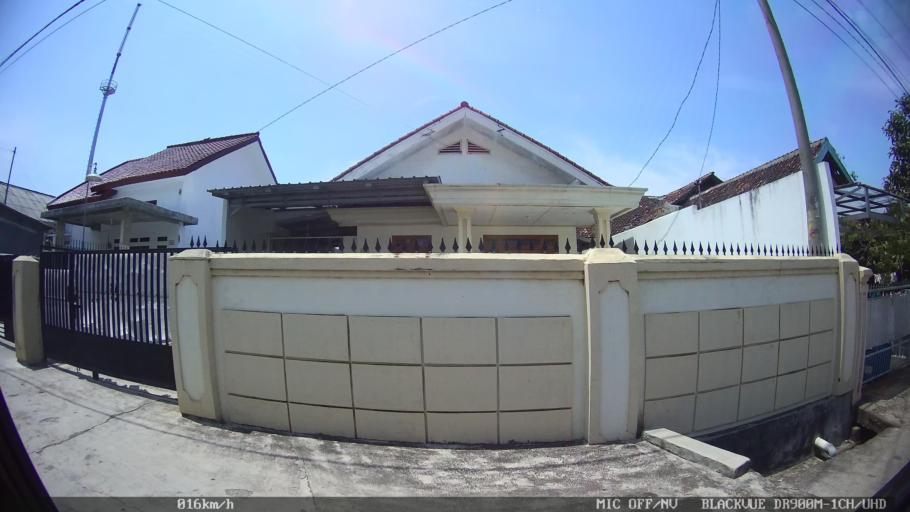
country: ID
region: Lampung
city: Bandarlampung
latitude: -5.4055
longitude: 105.2688
